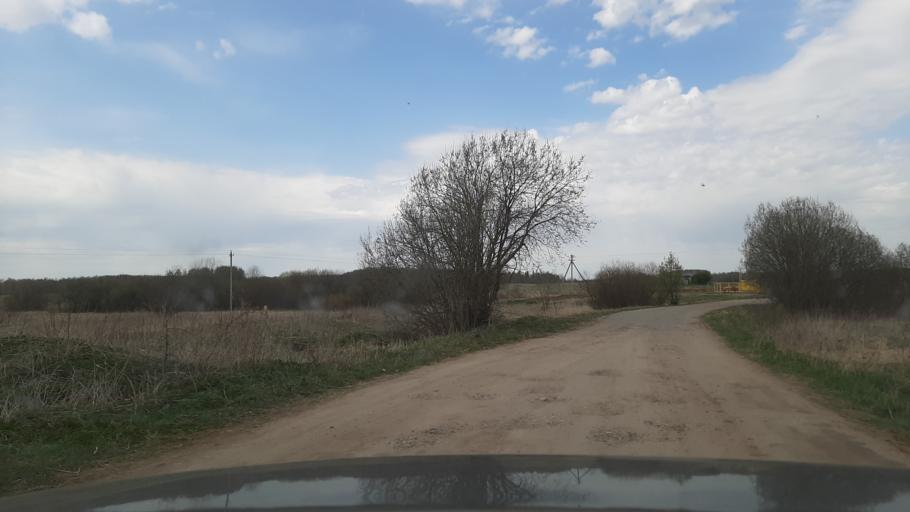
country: RU
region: Ivanovo
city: Furmanov
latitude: 57.3184
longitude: 41.1565
